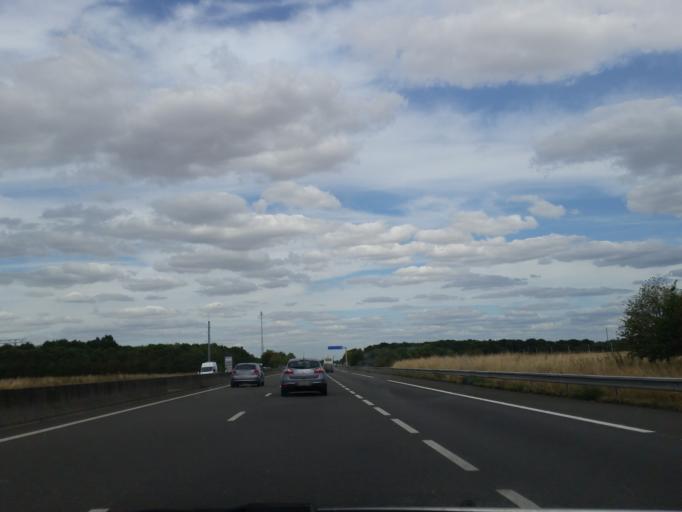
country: FR
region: Centre
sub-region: Departement du Loir-et-Cher
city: Herbault
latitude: 47.6035
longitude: 1.1146
